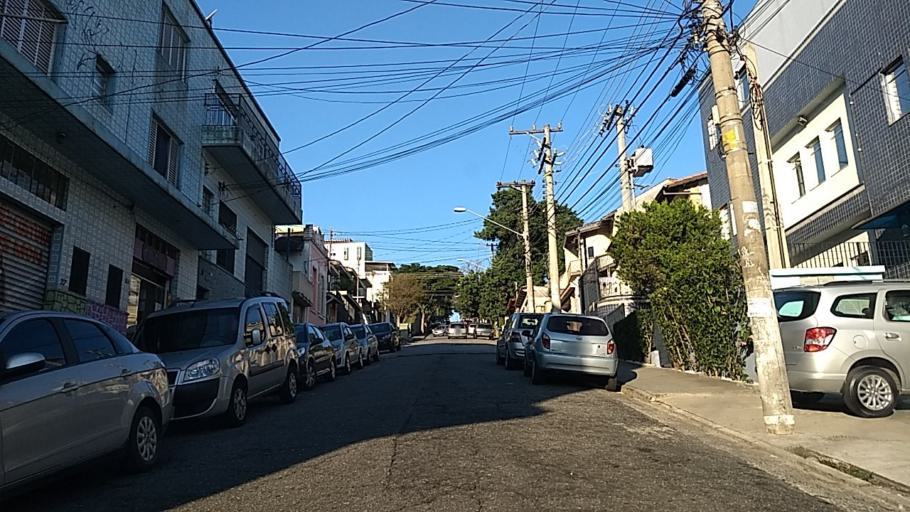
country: BR
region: Sao Paulo
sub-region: Sao Paulo
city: Sao Paulo
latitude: -23.4918
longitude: -46.6087
